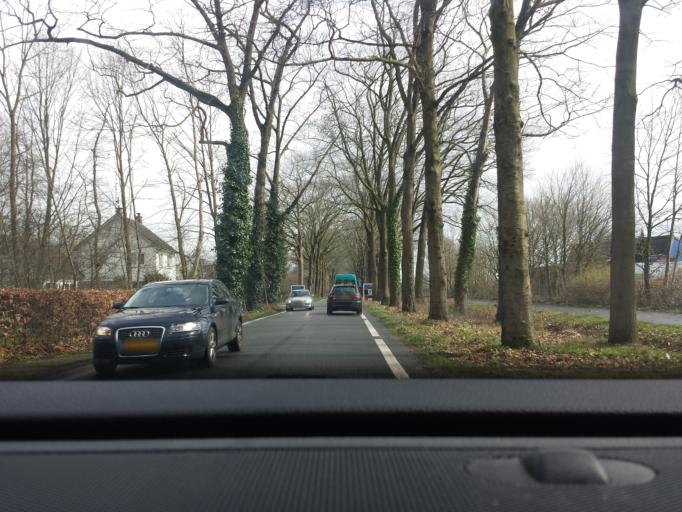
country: NL
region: Gelderland
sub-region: Gemeente Bronckhorst
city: Zelhem
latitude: 52.0055
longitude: 6.3629
